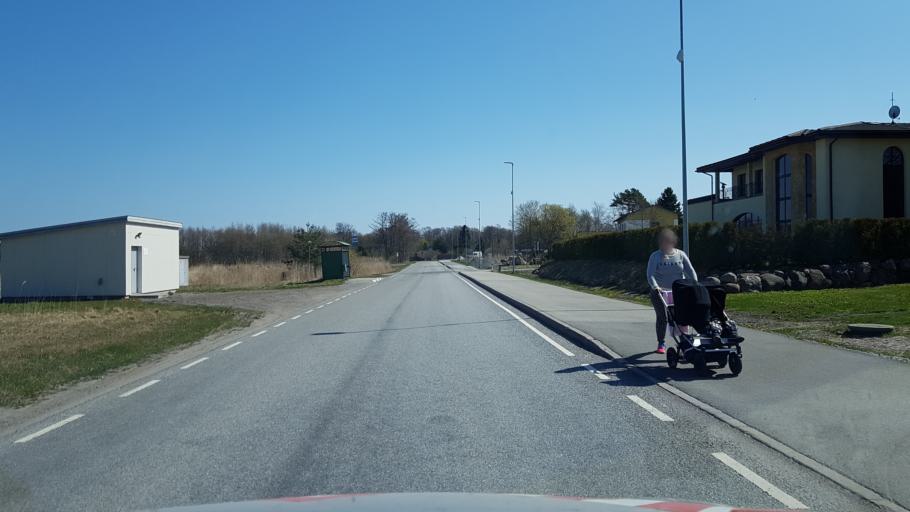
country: EE
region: Harju
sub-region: Viimsi vald
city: Viimsi
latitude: 59.5481
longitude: 24.8745
